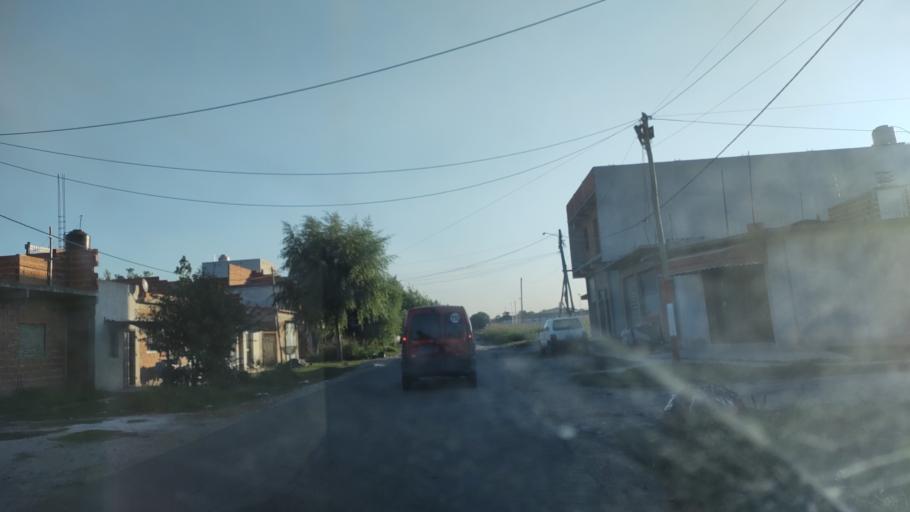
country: AR
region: Buenos Aires
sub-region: Partido de La Plata
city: La Plata
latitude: -34.9683
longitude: -57.9688
